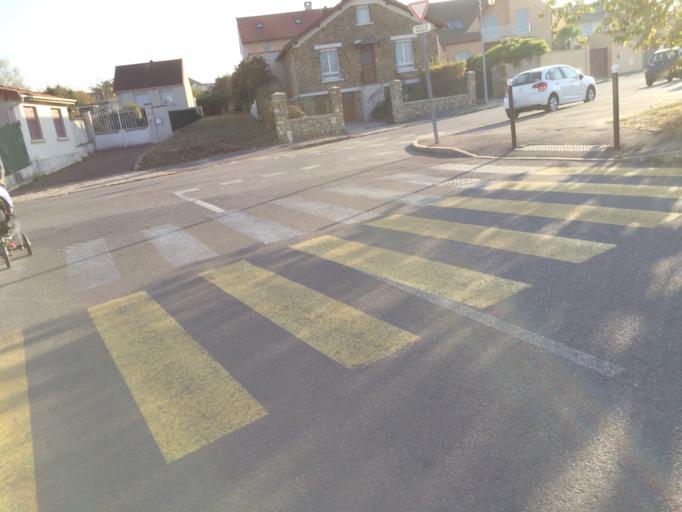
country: FR
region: Ile-de-France
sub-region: Departement de l'Essonne
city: Nozay
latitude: 48.6621
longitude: 2.2418
